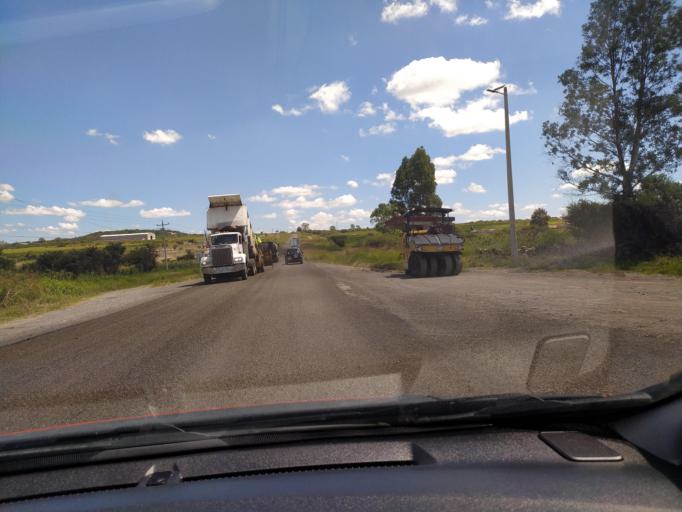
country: MX
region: Jalisco
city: San Julian
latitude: 21.0022
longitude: -102.0903
